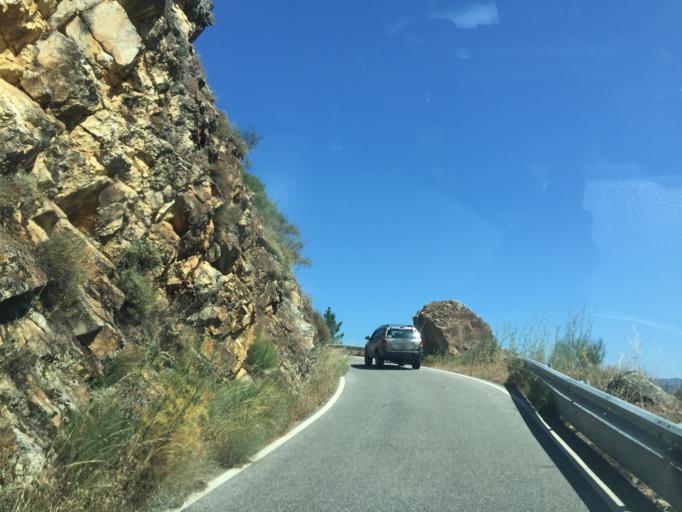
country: PT
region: Coimbra
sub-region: Pampilhosa da Serra
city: Pampilhosa da Serra
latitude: 40.0365
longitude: -7.8091
